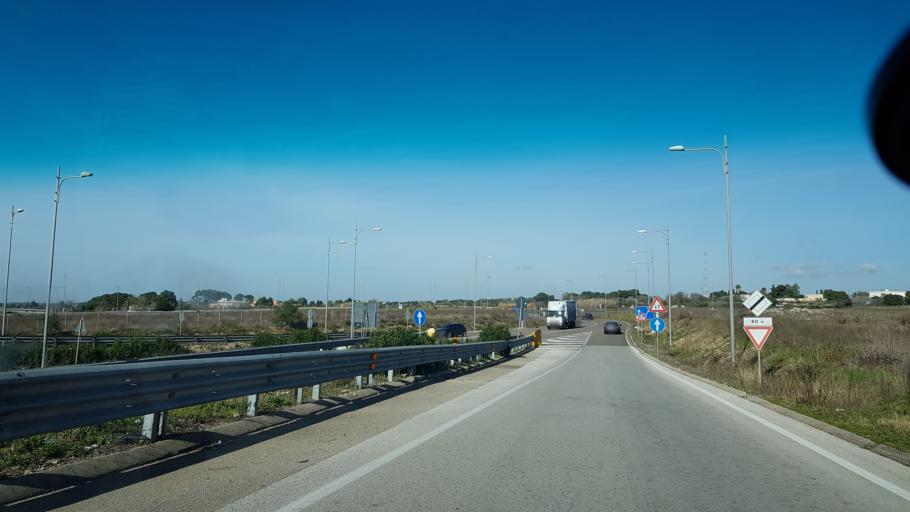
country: IT
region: Apulia
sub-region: Provincia di Lecce
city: Lequile
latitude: 40.3270
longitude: 18.1533
